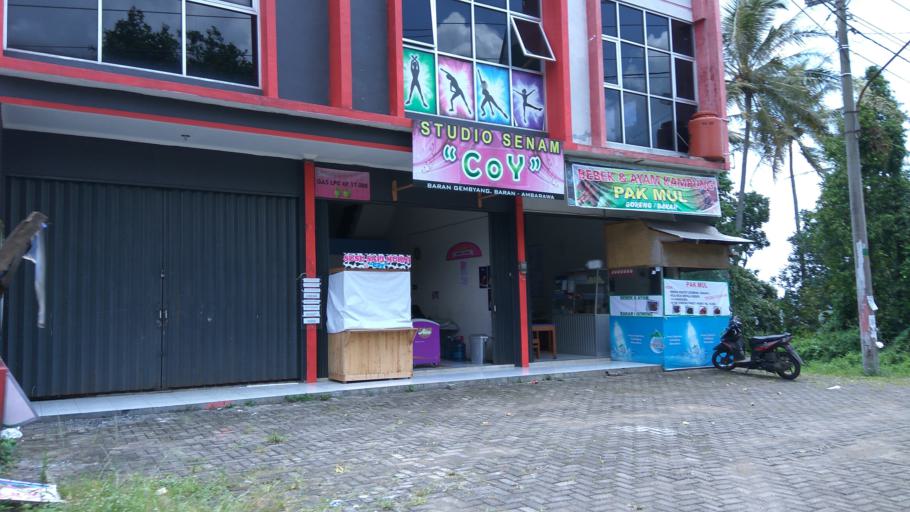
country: ID
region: Central Java
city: Ambarawa
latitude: -7.2450
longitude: 110.3983
